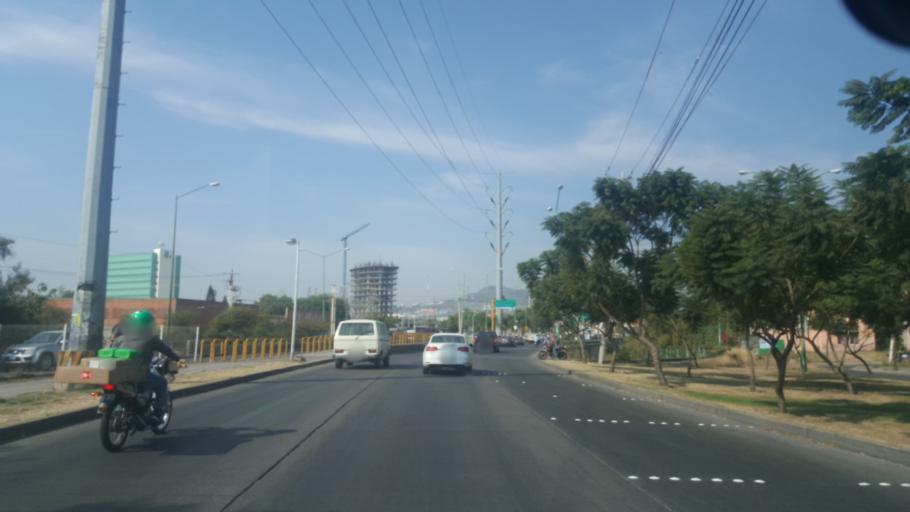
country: MX
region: Guanajuato
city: Leon
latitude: 21.1542
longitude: -101.6814
